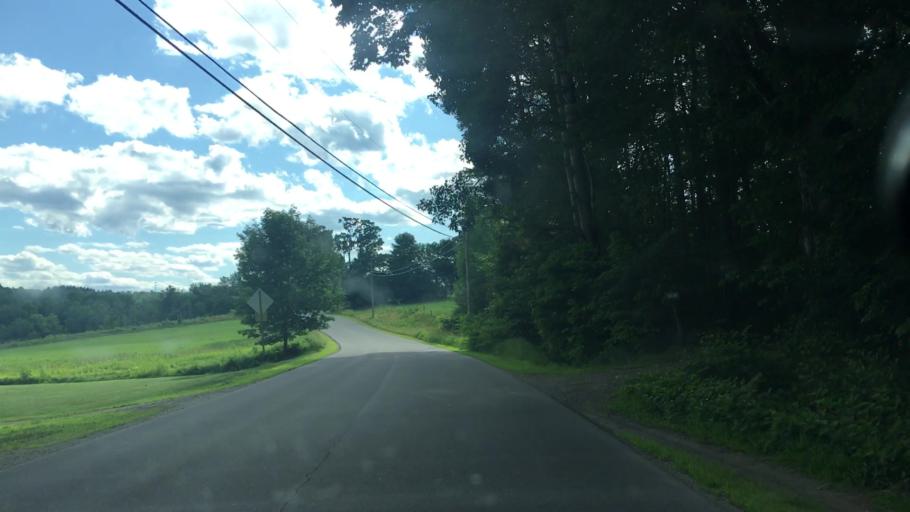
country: US
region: Maine
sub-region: Franklin County
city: Farmington
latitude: 44.6495
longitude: -70.1814
